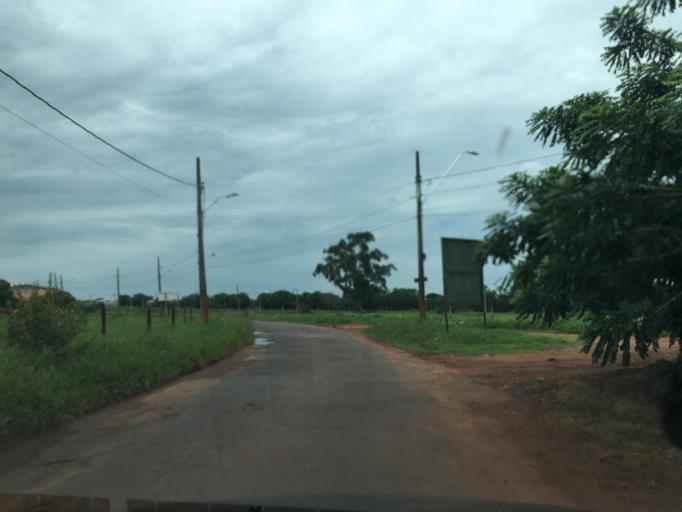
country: BR
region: Minas Gerais
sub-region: Uberlandia
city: Uberlandia
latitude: -18.8640
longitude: -48.2220
